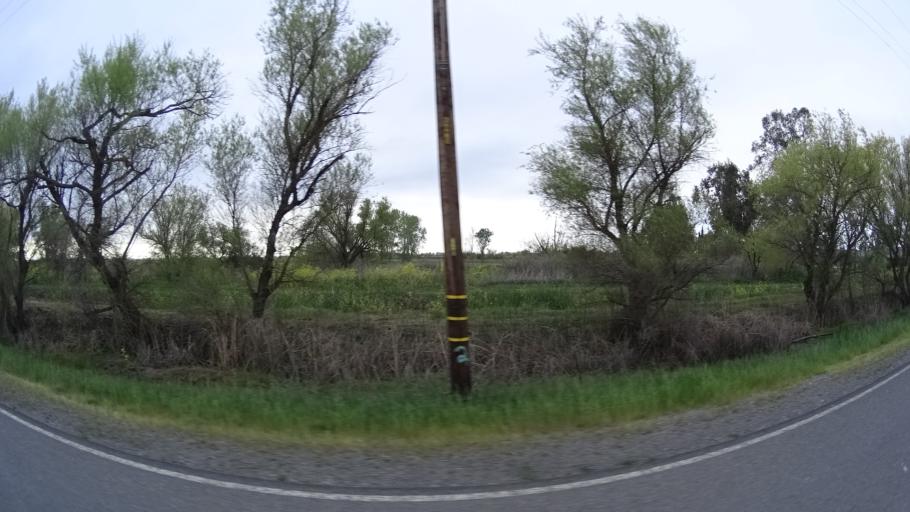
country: US
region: California
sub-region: Glenn County
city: Willows
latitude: 39.4064
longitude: -122.1147
